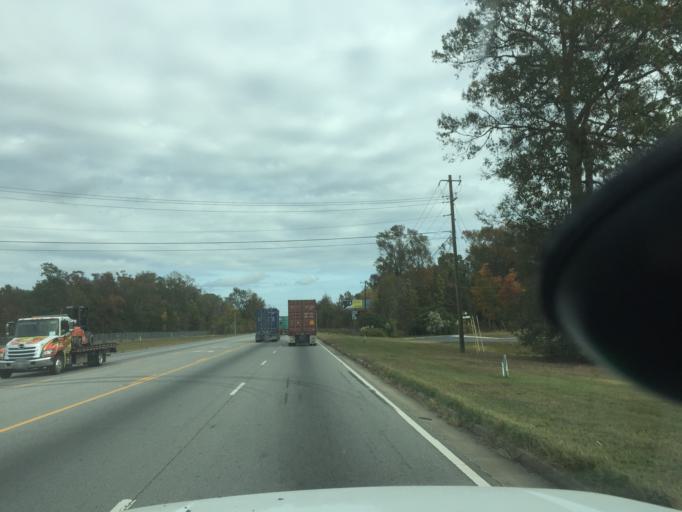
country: US
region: Georgia
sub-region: Chatham County
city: Garden City
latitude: 32.1202
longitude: -81.1885
